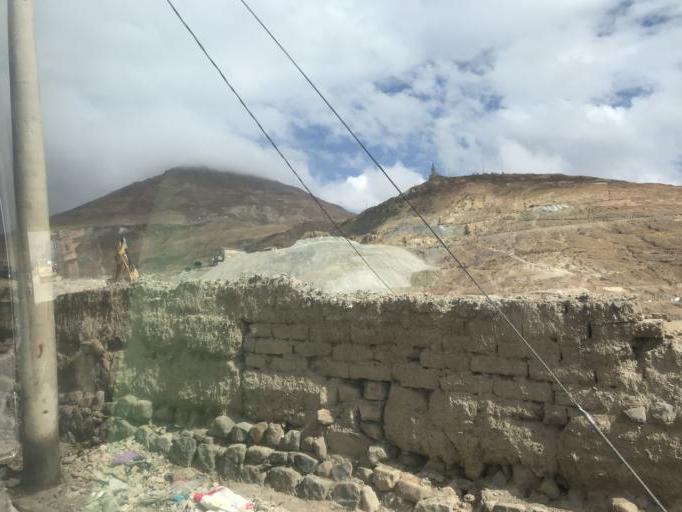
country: BO
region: Potosi
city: Potosi
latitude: -19.6004
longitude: -65.7463
